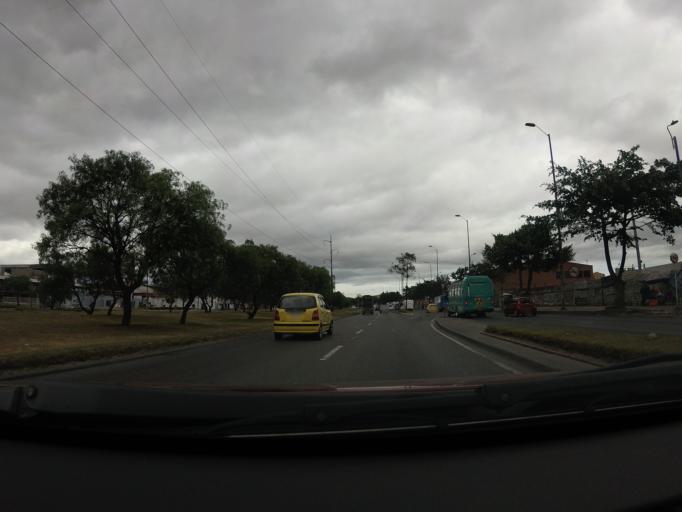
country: CO
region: Bogota D.C.
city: Bogota
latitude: 4.6468
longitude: -74.1300
